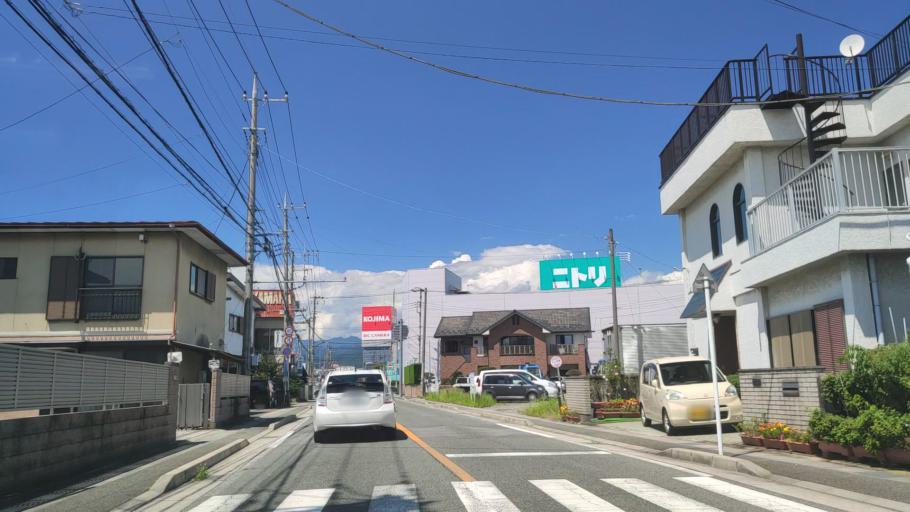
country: JP
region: Yamanashi
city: Kofu-shi
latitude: 35.6316
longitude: 138.5713
